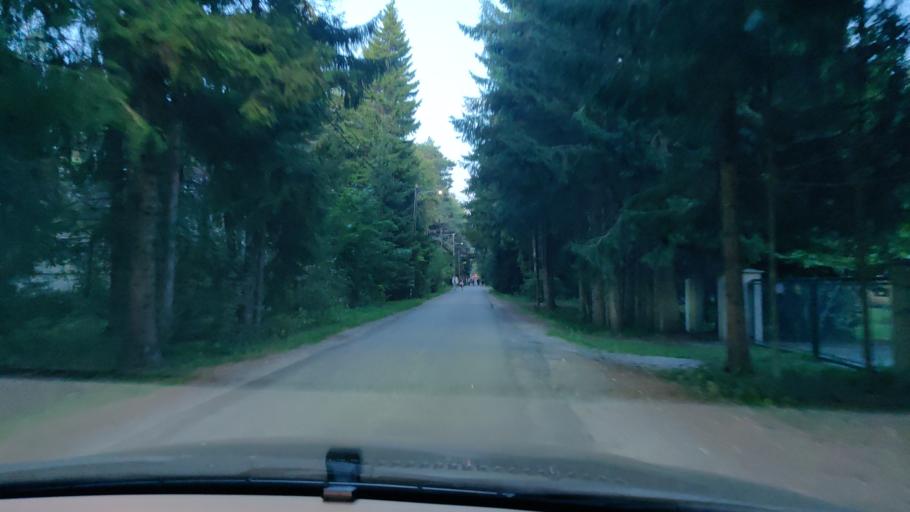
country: EE
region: Harju
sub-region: Keila linn
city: Keila
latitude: 59.3468
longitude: 24.2579
